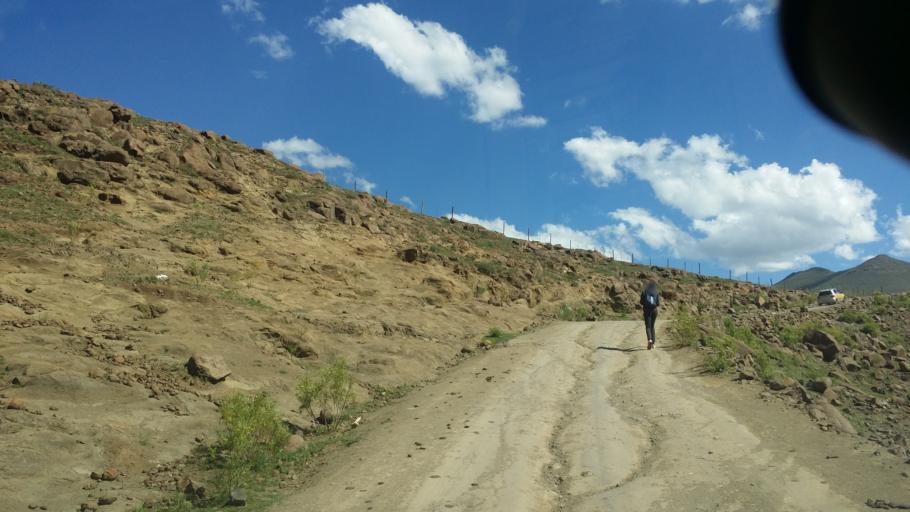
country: LS
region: Mokhotlong
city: Mokhotlong
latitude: -29.2749
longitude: 29.0678
